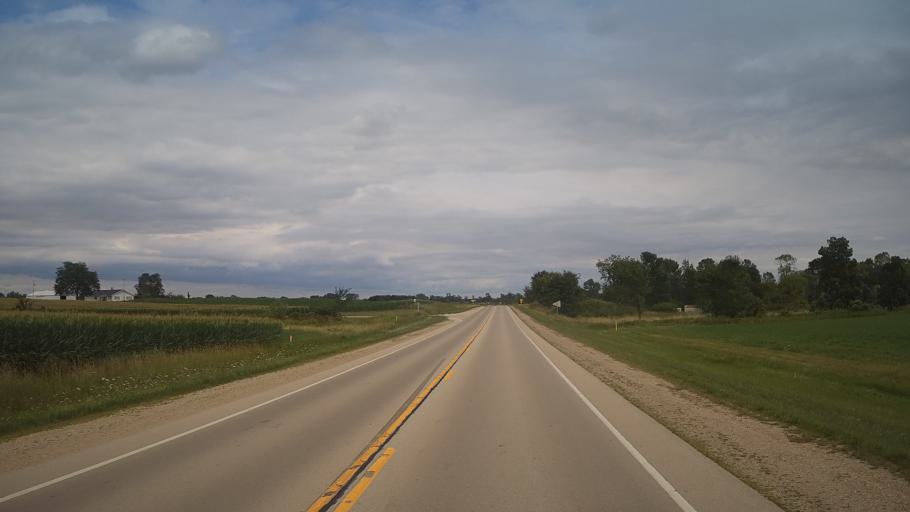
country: US
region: Wisconsin
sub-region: Green Lake County
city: Berlin
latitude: 44.0454
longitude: -88.9785
